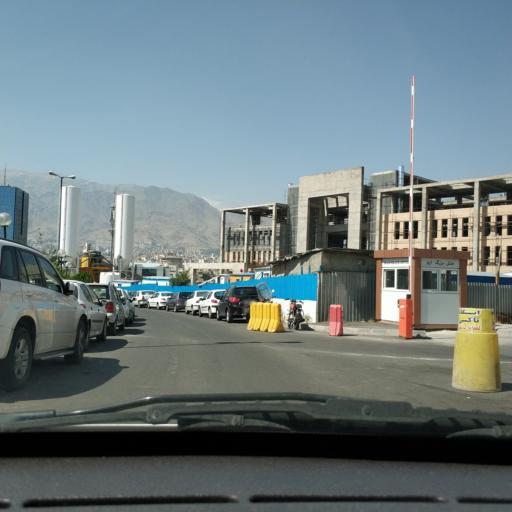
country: IR
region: Tehran
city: Tajrish
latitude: 35.7528
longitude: 51.4357
